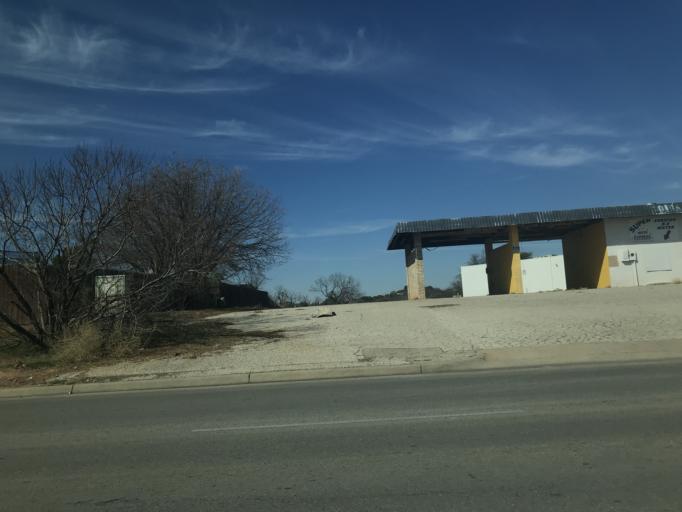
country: US
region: Texas
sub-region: Tom Green County
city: San Angelo
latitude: 31.4326
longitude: -100.4815
